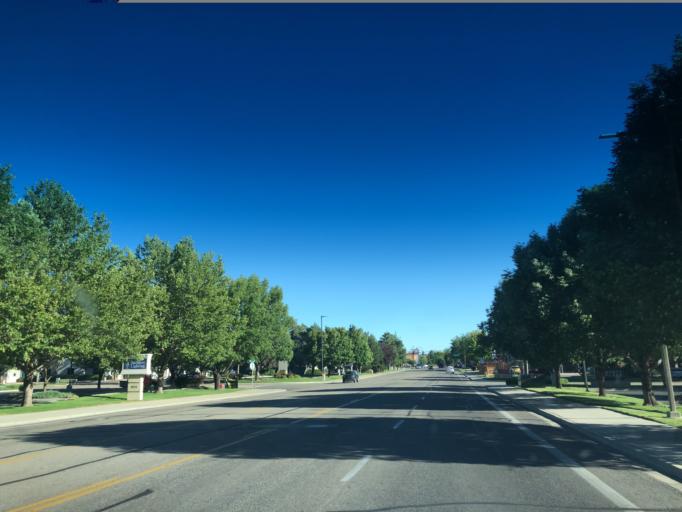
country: US
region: Idaho
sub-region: Ada County
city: Garden City
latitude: 43.6135
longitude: -116.2843
